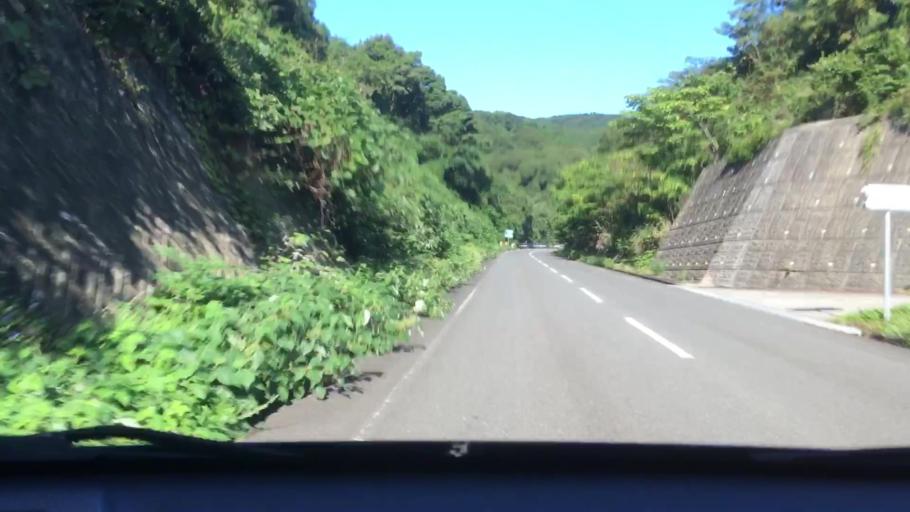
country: JP
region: Nagasaki
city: Sasebo
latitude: 32.9967
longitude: 129.7106
